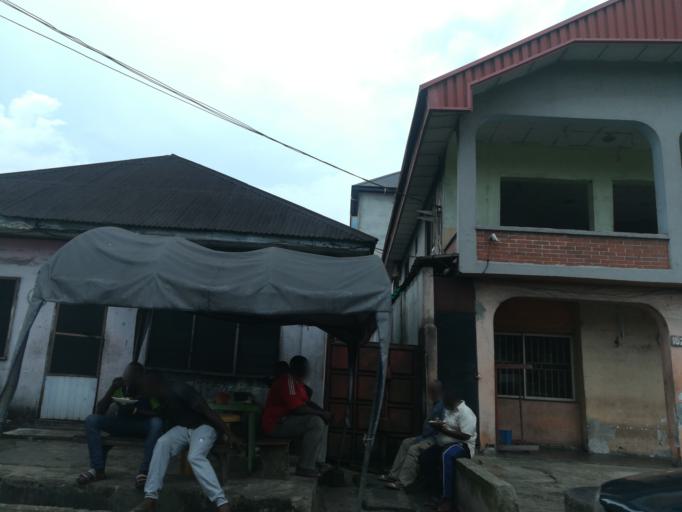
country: NG
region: Rivers
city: Port Harcourt
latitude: 4.7607
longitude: 7.0290
